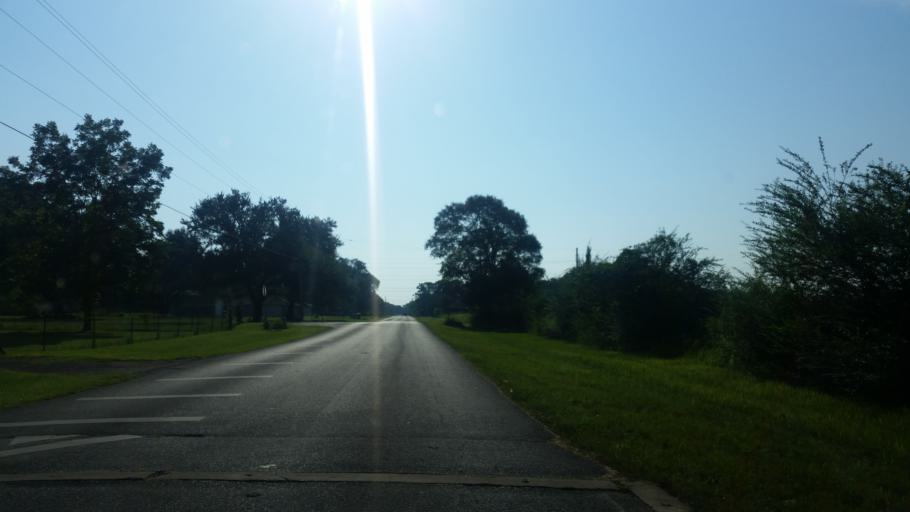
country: US
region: Florida
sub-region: Escambia County
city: Bellview
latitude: 30.4760
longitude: -87.3182
